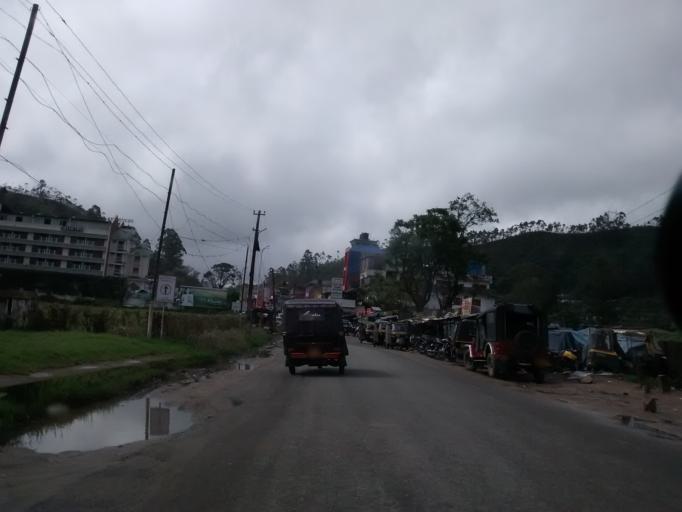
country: IN
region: Kerala
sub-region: Idukki
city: Munnar
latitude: 10.0768
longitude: 77.0630
